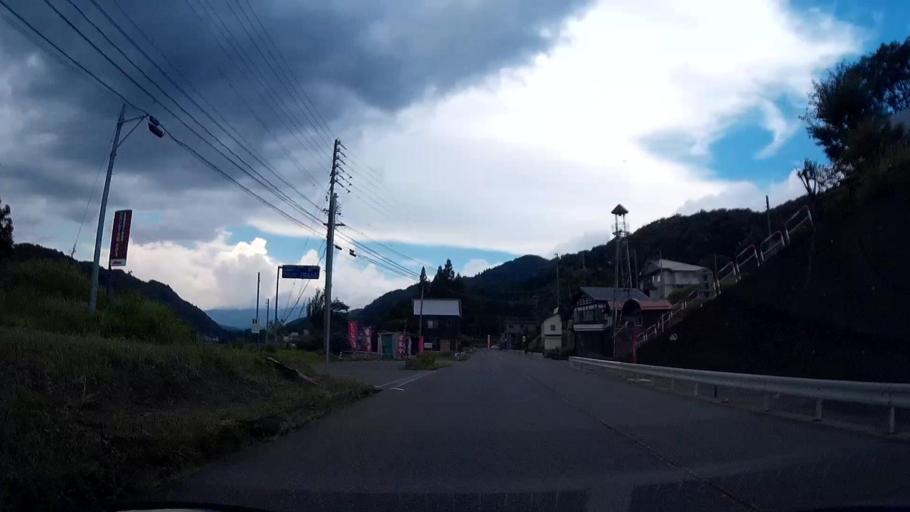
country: JP
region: Nagano
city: Iiyama
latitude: 36.9852
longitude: 138.5315
